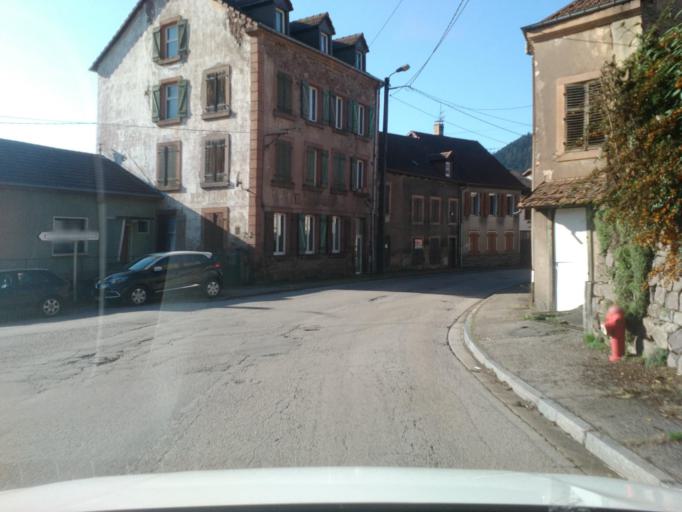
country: FR
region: Lorraine
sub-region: Departement des Vosges
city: Senones
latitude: 48.4047
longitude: 6.9964
